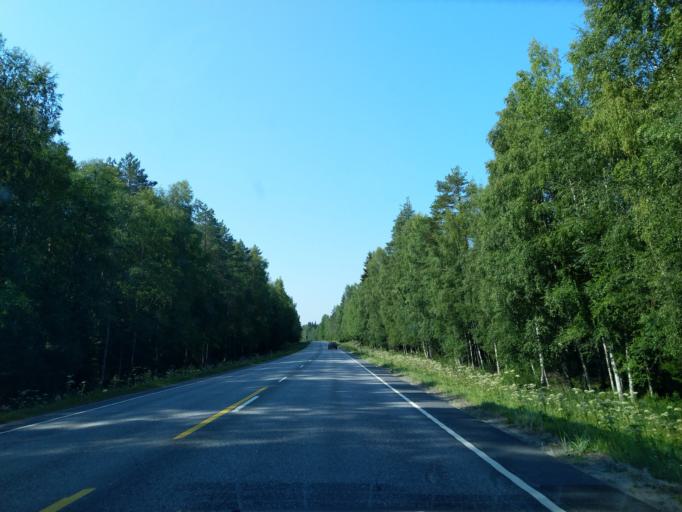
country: FI
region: Satakunta
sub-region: Pori
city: Noormarkku
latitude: 61.6147
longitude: 21.8944
